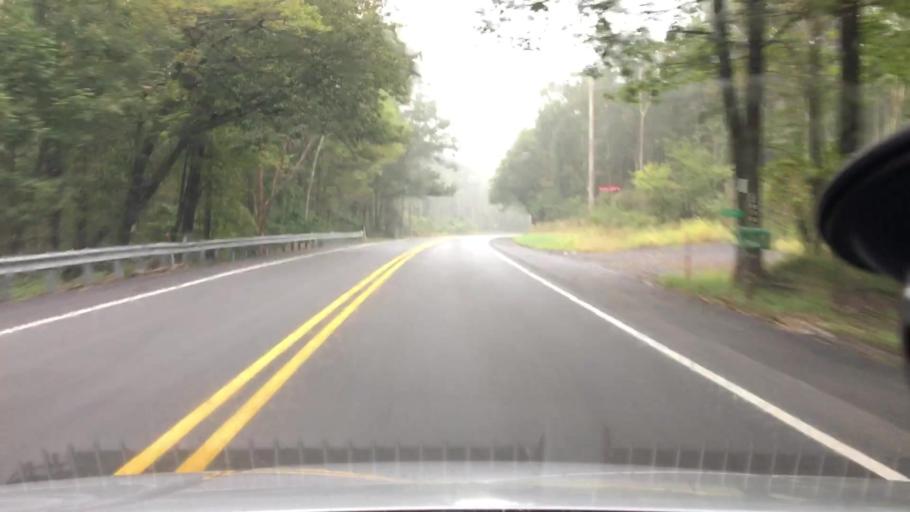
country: US
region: Pennsylvania
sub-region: Monroe County
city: Mount Pocono
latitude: 41.1292
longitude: -75.3301
